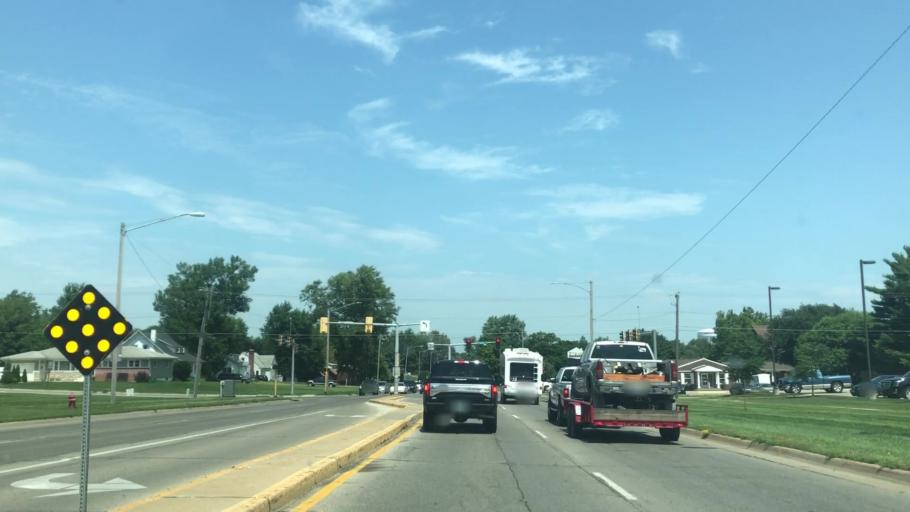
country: US
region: Iowa
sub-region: Marshall County
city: Marshalltown
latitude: 42.0276
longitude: -92.9126
